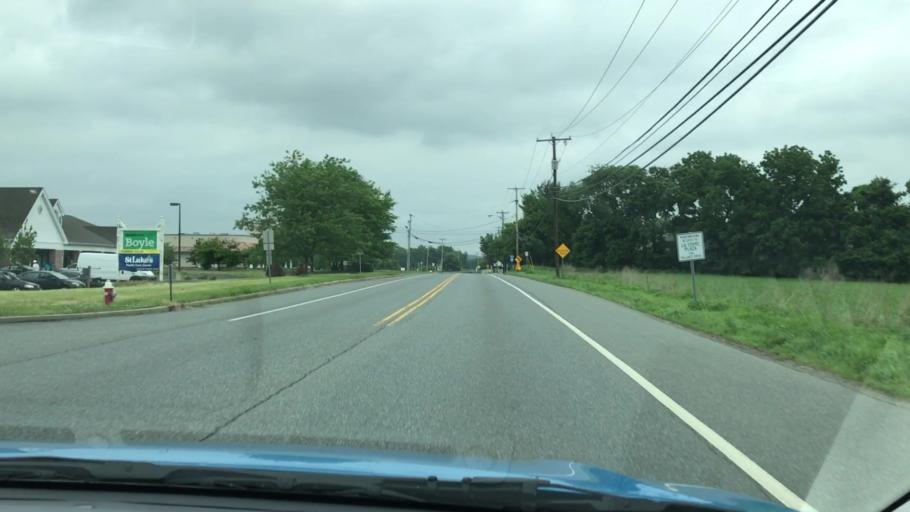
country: US
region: New Jersey
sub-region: Warren County
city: Belvidere
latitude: 40.8041
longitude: -75.0772
